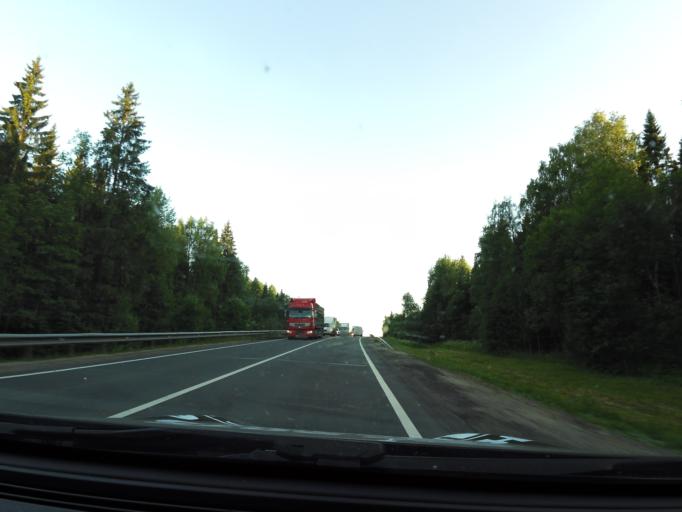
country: RU
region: Jaroslavl
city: Prechistoye
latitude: 58.4986
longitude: 40.3391
